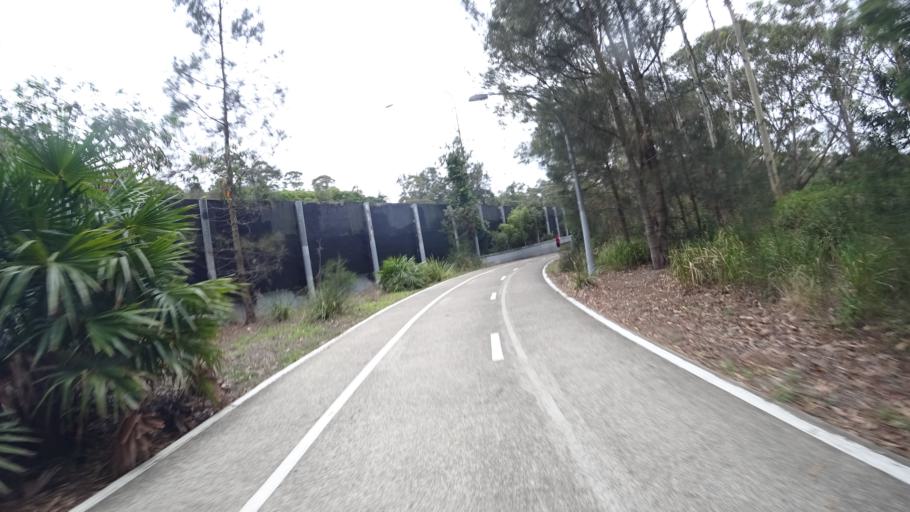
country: AU
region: New South Wales
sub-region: North Sydney
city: St Leonards
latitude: -33.8125
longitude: 151.1958
